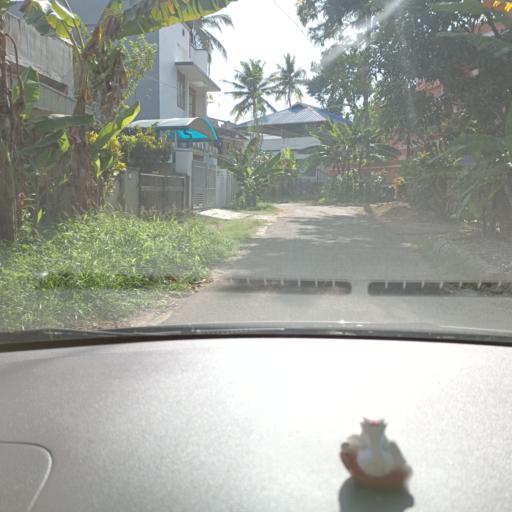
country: IN
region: Kerala
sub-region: Thiruvananthapuram
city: Nedumangad
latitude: 8.6076
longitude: 76.9959
